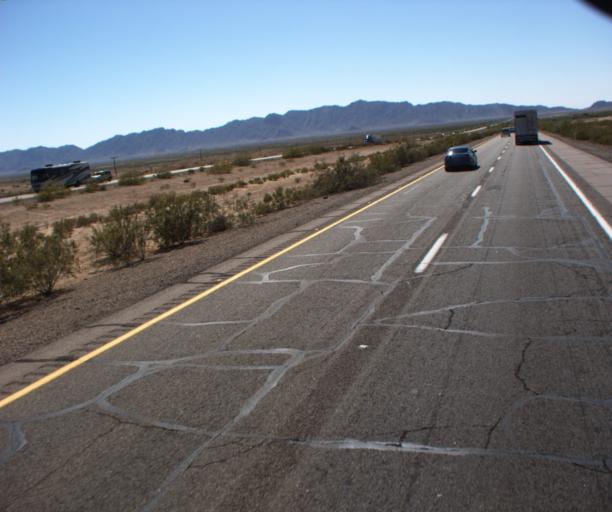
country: US
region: Arizona
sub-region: Yuma County
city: Wellton
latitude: 32.7585
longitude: -113.6420
